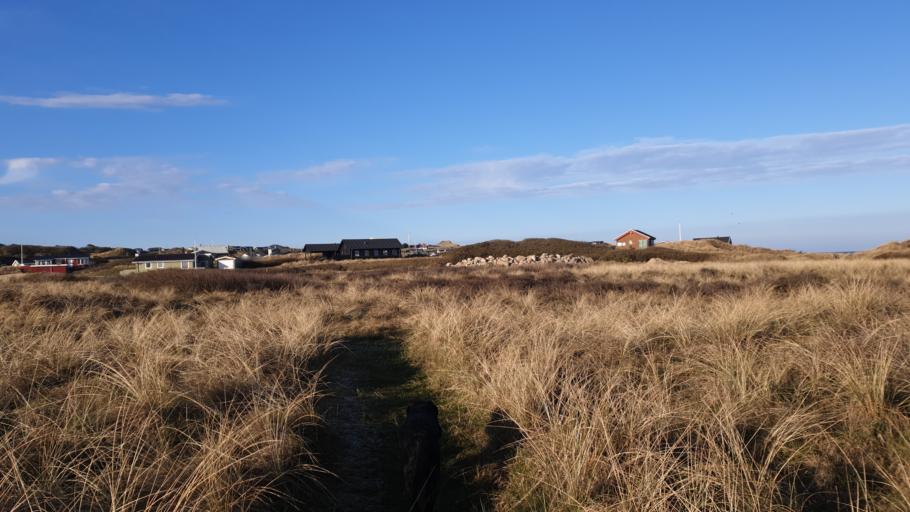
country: DK
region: North Denmark
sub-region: Hjorring Kommune
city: Hjorring
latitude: 57.4859
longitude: 9.8133
